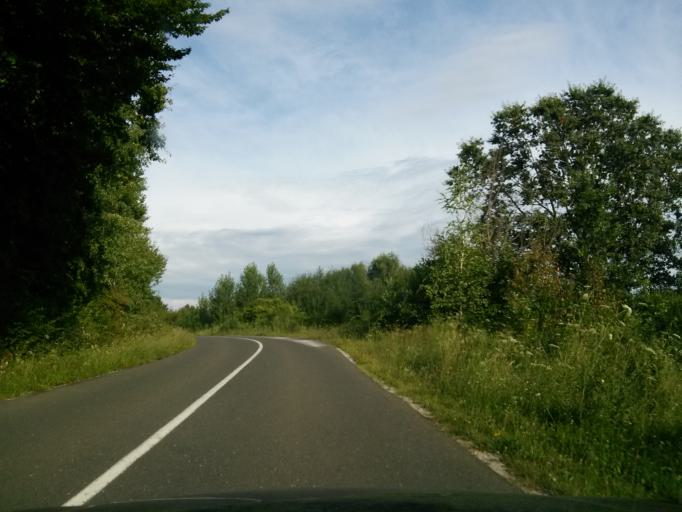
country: HR
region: Sisacko-Moslavacka
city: Gvozd
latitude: 45.4789
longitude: 15.9086
